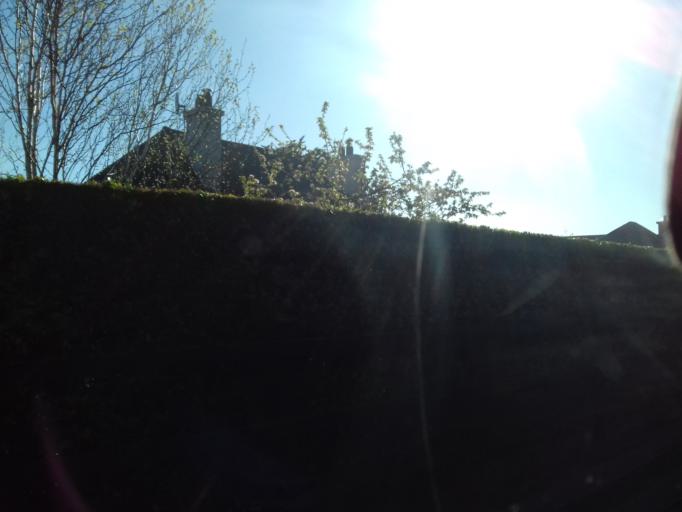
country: IE
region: Leinster
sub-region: Fingal County
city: Howth
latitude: 53.3653
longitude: -6.0774
